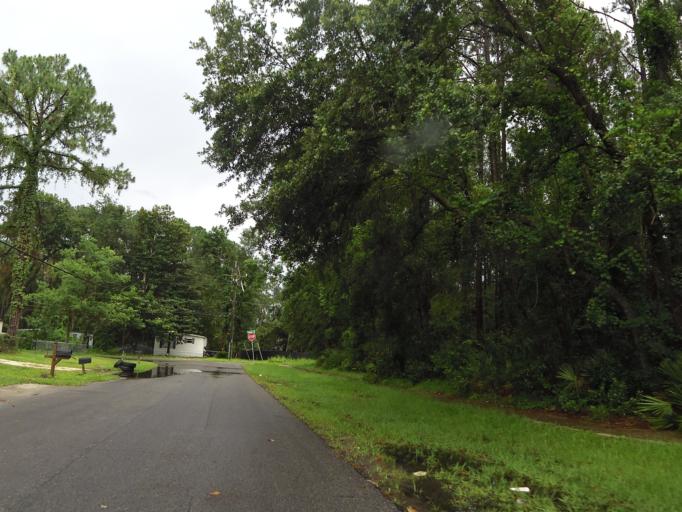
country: US
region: Florida
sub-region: Duval County
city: Jacksonville
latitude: 30.2762
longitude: -81.6355
